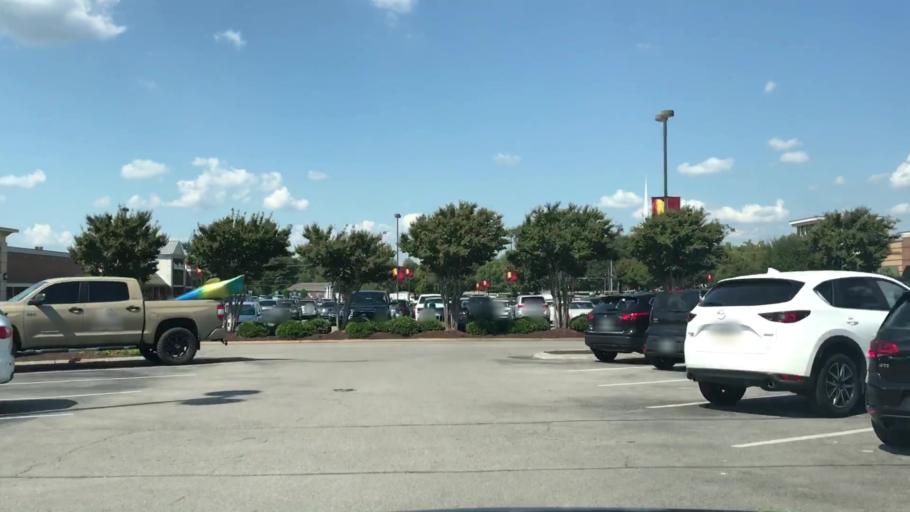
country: US
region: Tennessee
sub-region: Williamson County
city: Brentwood
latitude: 36.0258
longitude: -86.7893
